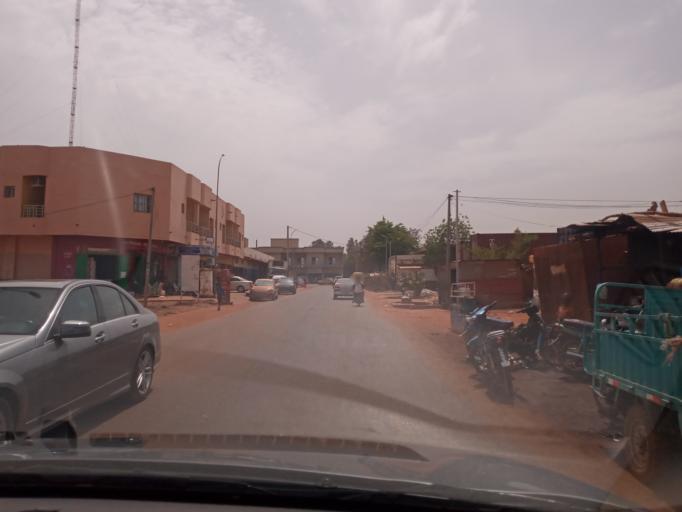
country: ML
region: Bamako
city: Bamako
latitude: 12.6564
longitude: -7.9352
